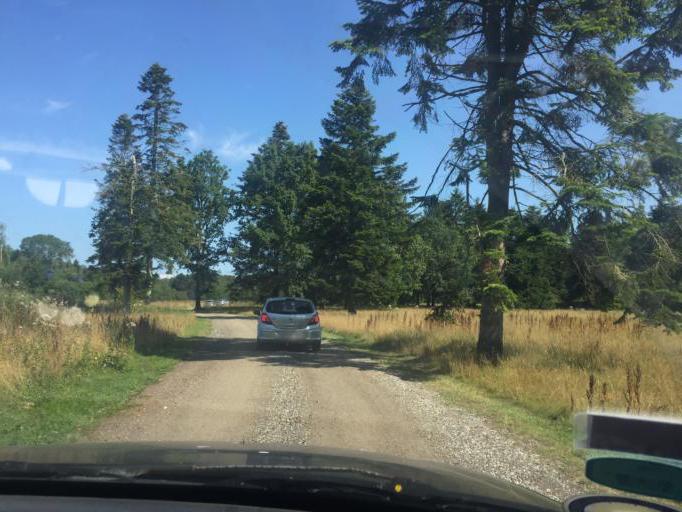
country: DK
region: Zealand
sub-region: Lolland Kommune
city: Maribo
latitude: 54.8183
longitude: 11.4976
